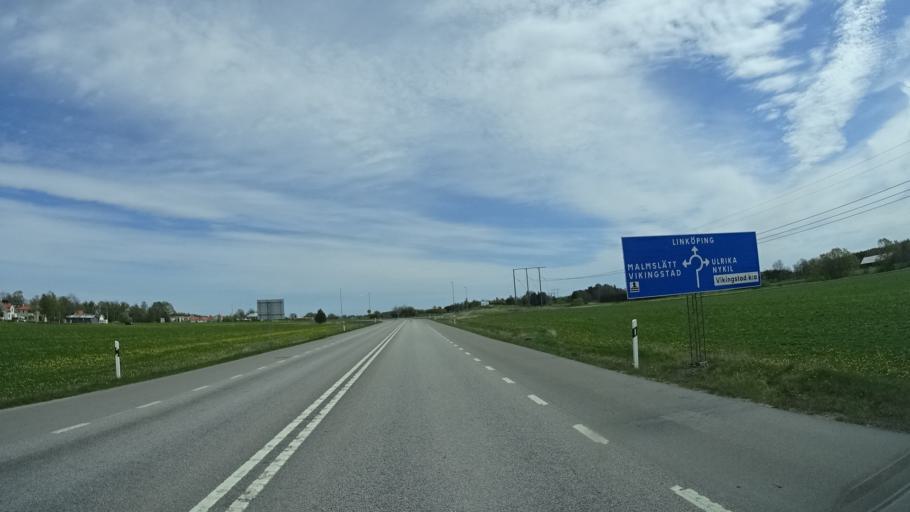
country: SE
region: OEstergoetland
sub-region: Linkopings Kommun
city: Vikingstad
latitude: 58.3764
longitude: 15.4321
